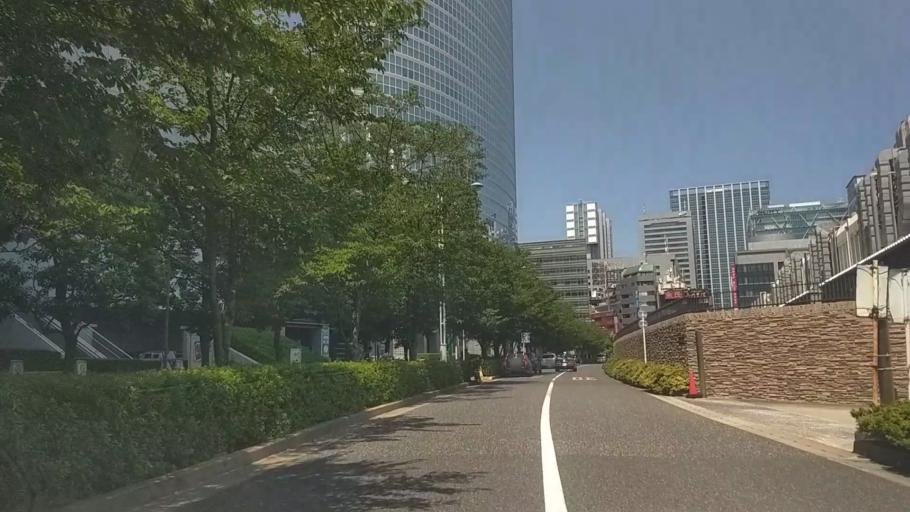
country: JP
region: Tokyo
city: Tokyo
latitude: 35.6262
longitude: 139.7425
